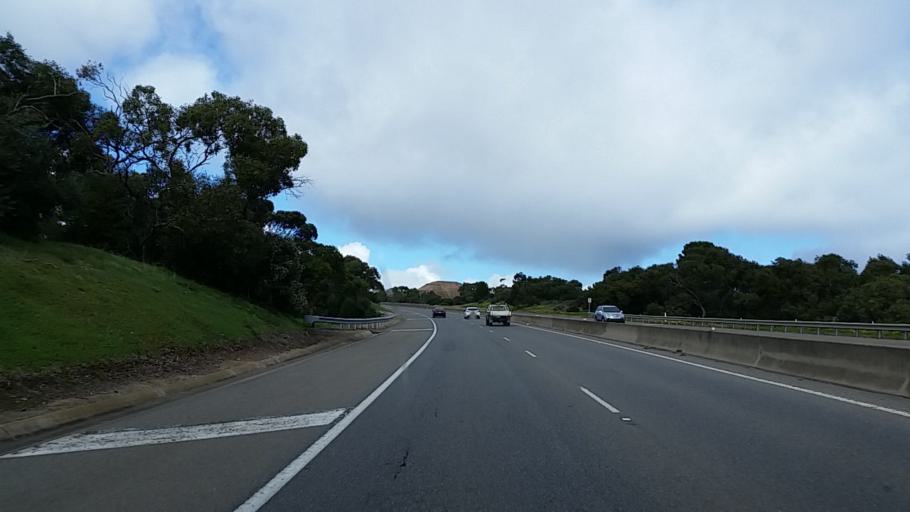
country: AU
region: South Australia
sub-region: Onkaparinga
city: Reynella
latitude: -35.0940
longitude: 138.4961
